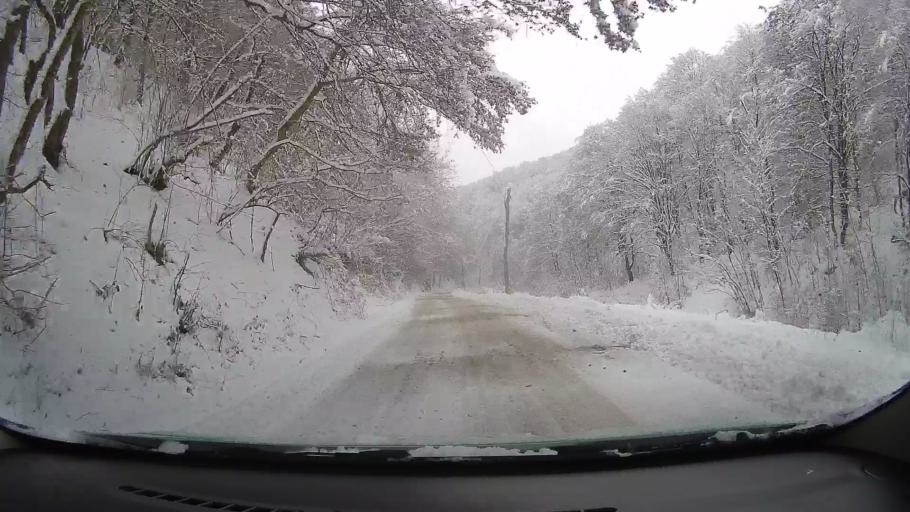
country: RO
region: Alba
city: Pianu de Sus
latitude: 45.8729
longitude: 23.4926
